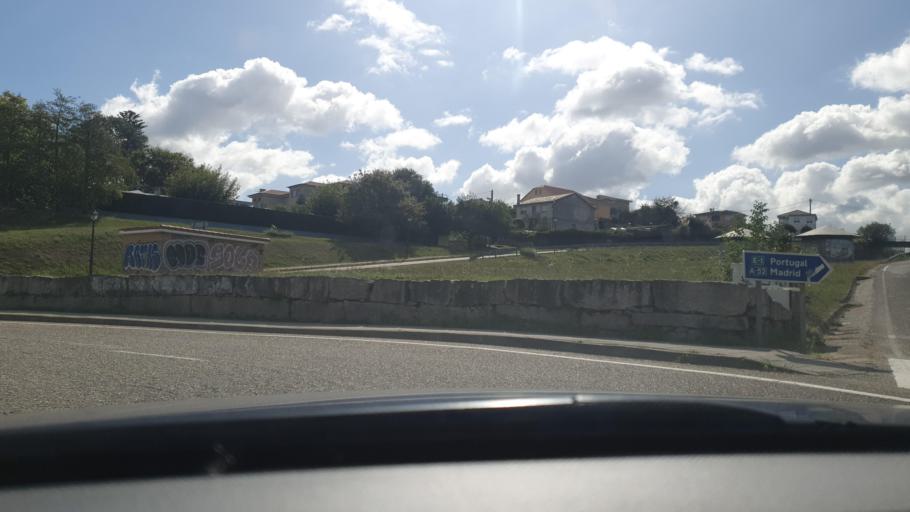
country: ES
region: Galicia
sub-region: Provincia de Pontevedra
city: Vigo
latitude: 42.2220
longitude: -8.7575
